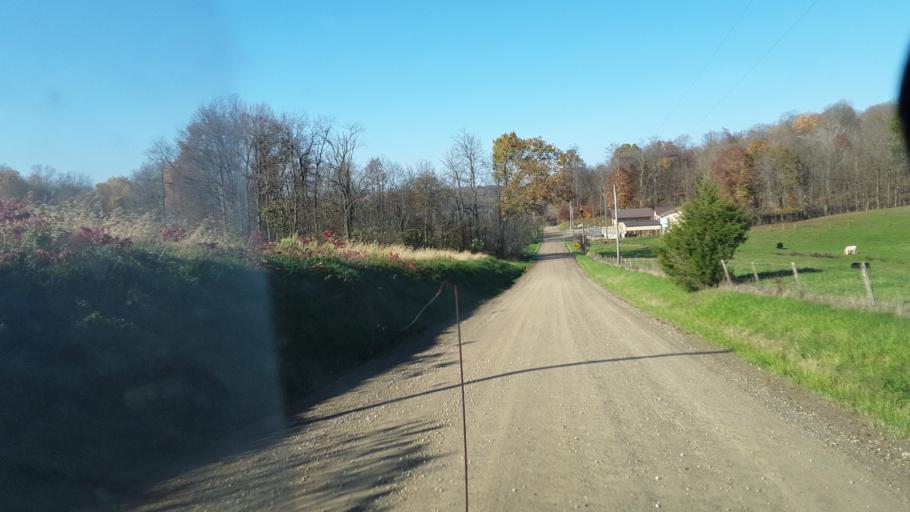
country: US
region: Ohio
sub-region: Knox County
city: Gambier
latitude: 40.5094
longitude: -82.4092
